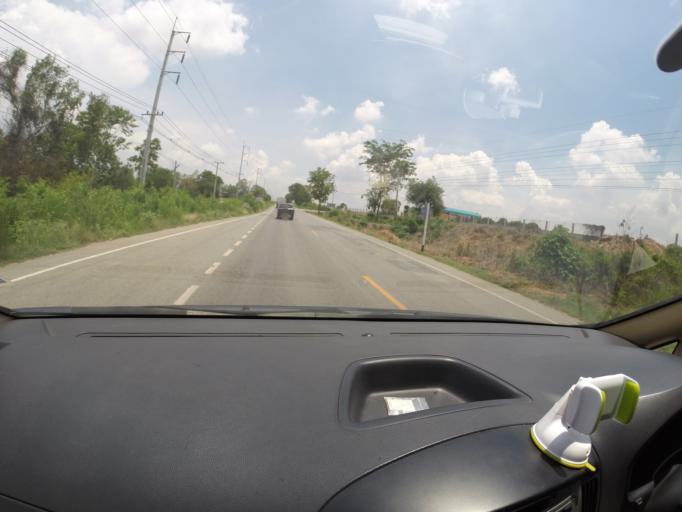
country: TH
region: Nakhon Ratchasima
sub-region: Amphoe Thepharak
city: Thepharak
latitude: 15.1270
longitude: 101.5514
